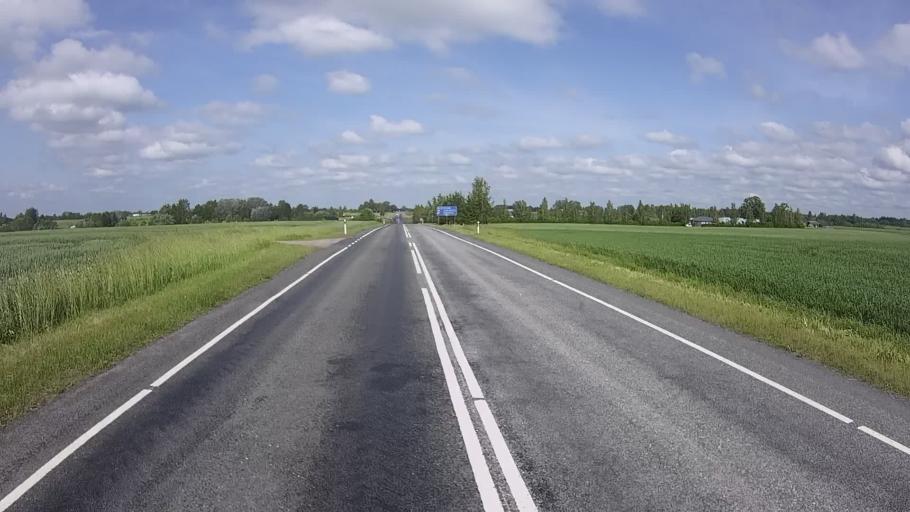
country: EE
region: Vorumaa
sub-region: Antsla vald
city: Vana-Antsla
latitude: 57.8829
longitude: 26.5343
